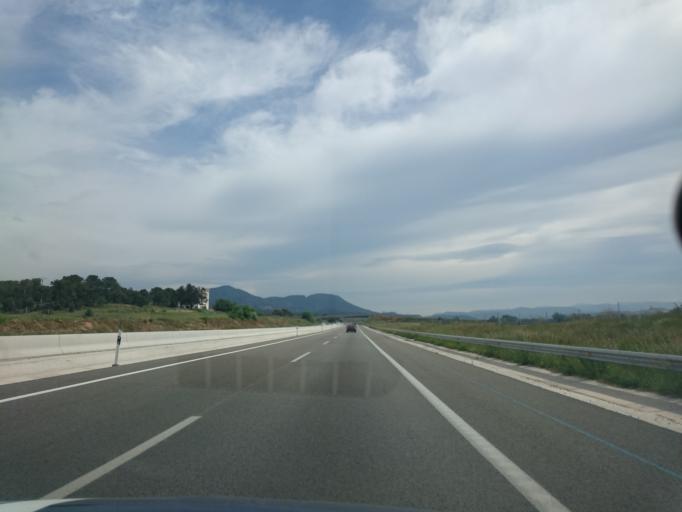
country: ES
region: Catalonia
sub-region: Provincia de Barcelona
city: Navarcles
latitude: 41.7885
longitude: 1.9125
